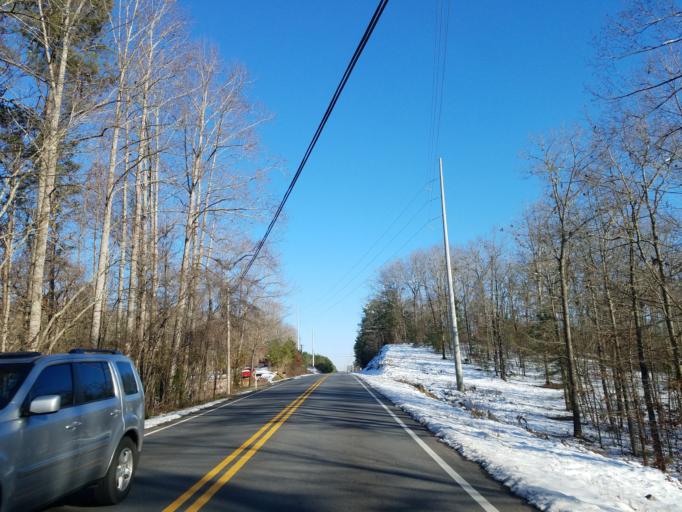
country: US
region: Georgia
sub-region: Dawson County
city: Dawsonville
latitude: 34.3539
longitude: -84.0862
